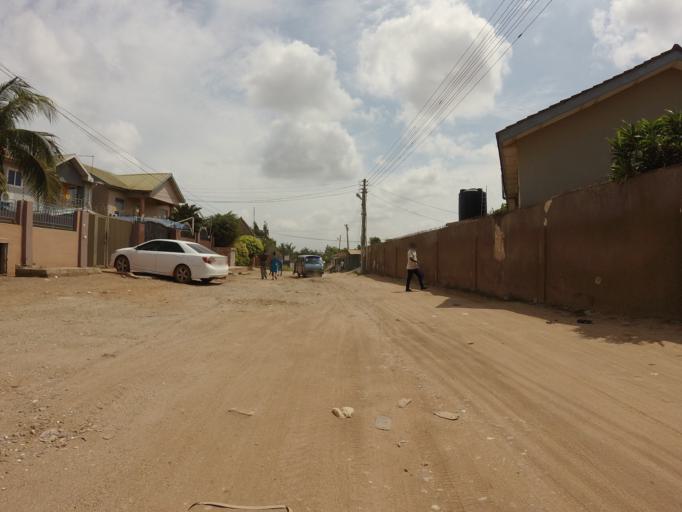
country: GH
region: Greater Accra
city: Dome
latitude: 5.6373
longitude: -0.2370
